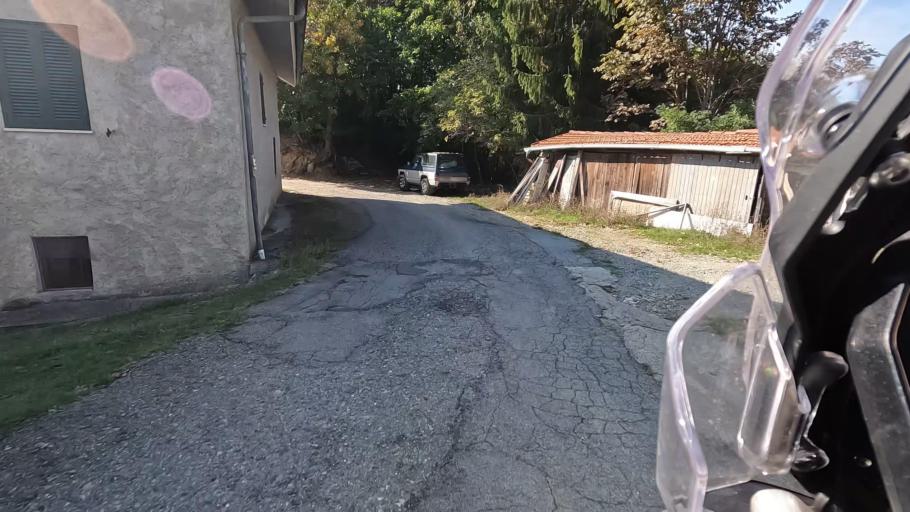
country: IT
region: Liguria
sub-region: Provincia di Savona
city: Urbe
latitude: 44.5285
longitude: 8.5431
